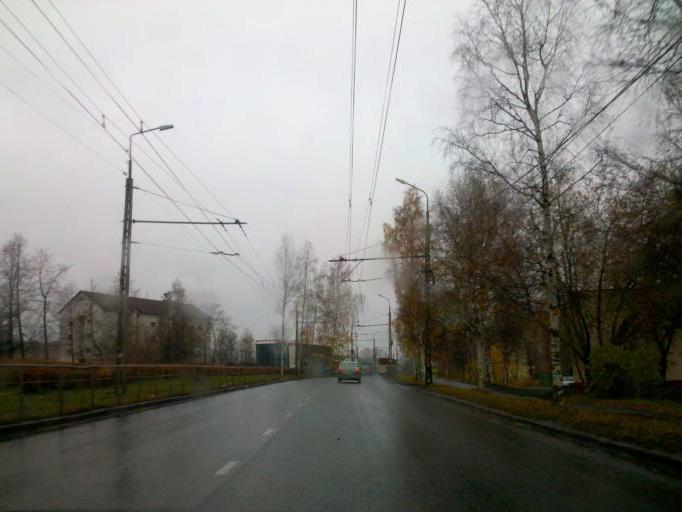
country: RU
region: Republic of Karelia
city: Petrozavodsk
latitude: 61.8000
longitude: 34.3192
